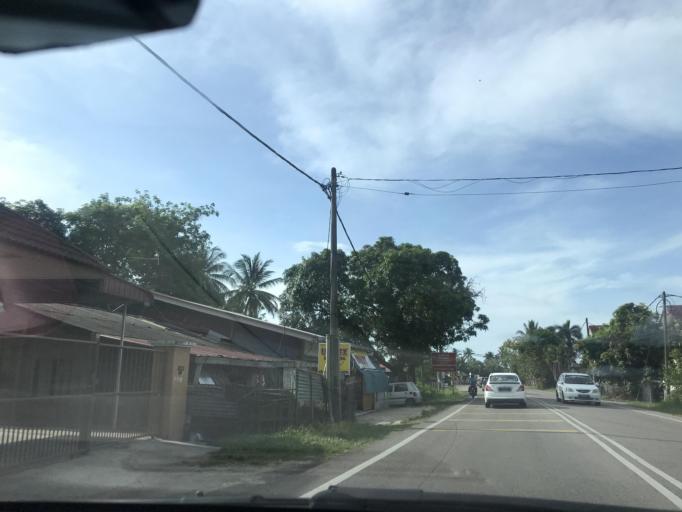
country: MY
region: Kelantan
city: Kota Bharu
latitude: 6.1311
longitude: 102.2016
